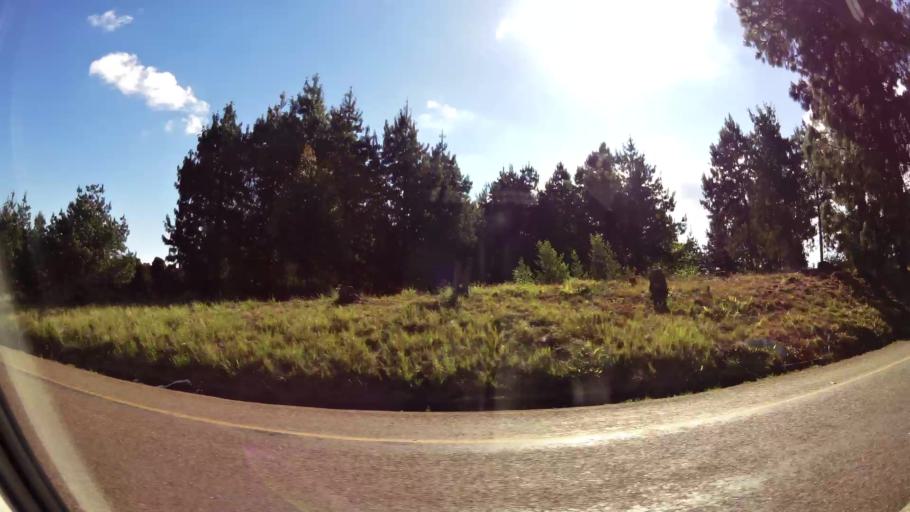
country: ZA
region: Limpopo
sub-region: Capricorn District Municipality
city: Mankoeng
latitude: -23.9017
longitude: 29.9924
